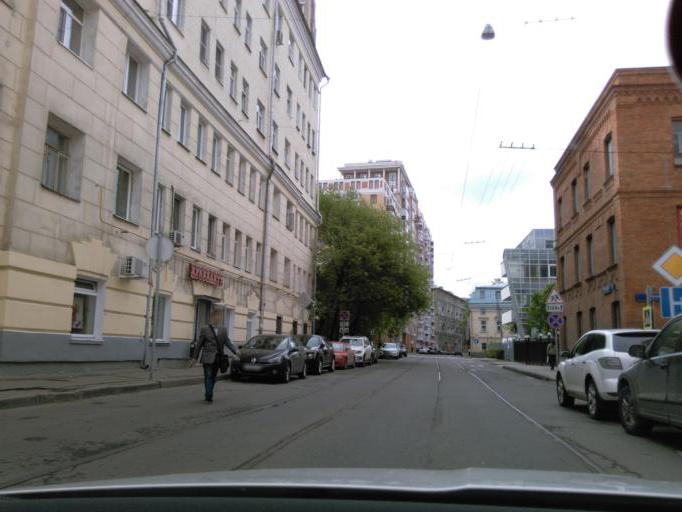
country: RU
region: Moscow
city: Mar'ina Roshcha
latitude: 55.7869
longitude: 37.6330
